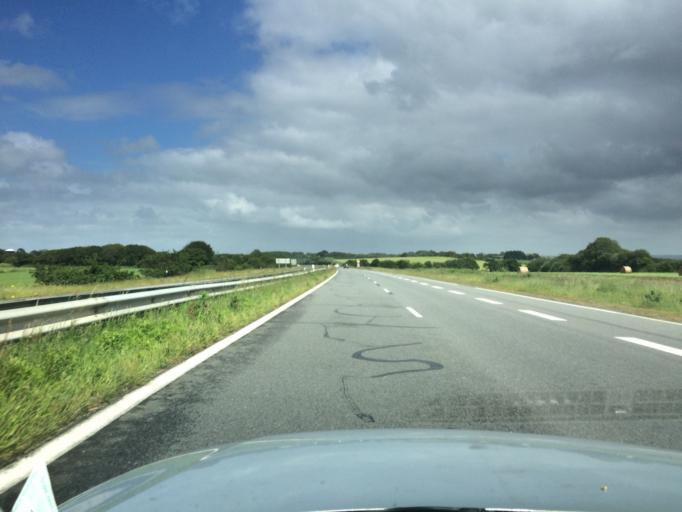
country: FR
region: Brittany
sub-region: Departement du Finistere
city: Gouesnou
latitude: 48.4341
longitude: -4.4384
